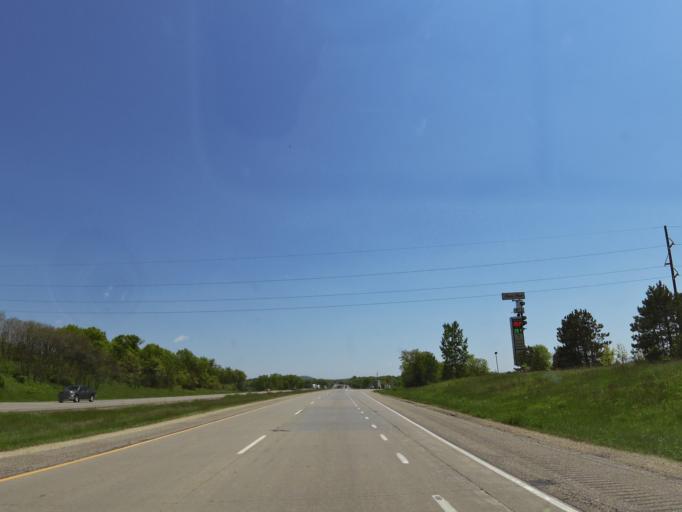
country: US
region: Wisconsin
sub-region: Juneau County
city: Mauston
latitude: 43.8004
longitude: -90.0603
